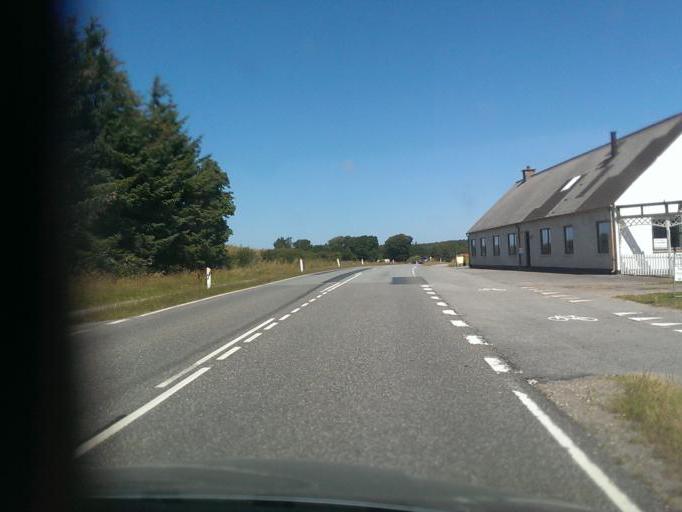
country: DK
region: North Denmark
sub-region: Jammerbugt Kommune
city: Pandrup
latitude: 57.3046
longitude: 9.6995
